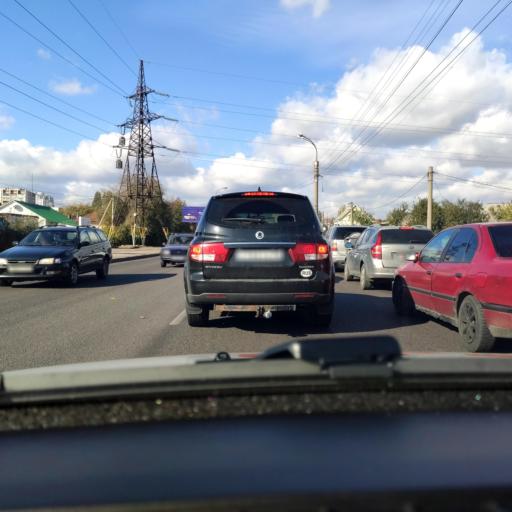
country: RU
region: Voronezj
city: Voronezh
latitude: 51.6422
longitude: 39.1559
